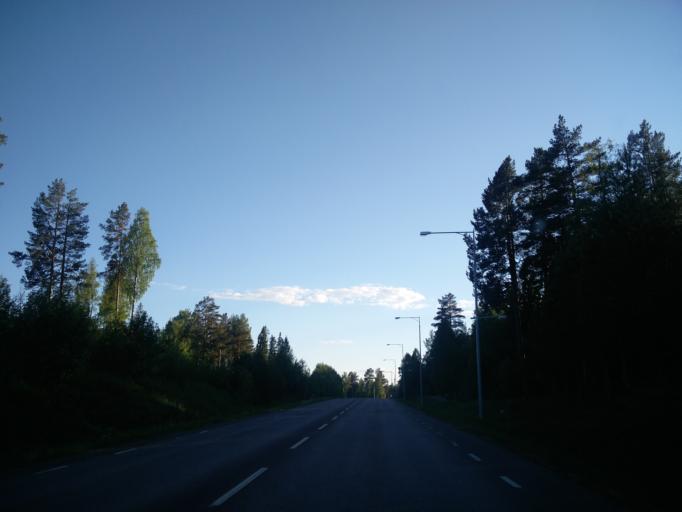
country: SE
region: Vaesternorrland
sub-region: Sundsvalls Kommun
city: Sundsvall
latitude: 62.4172
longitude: 17.2615
